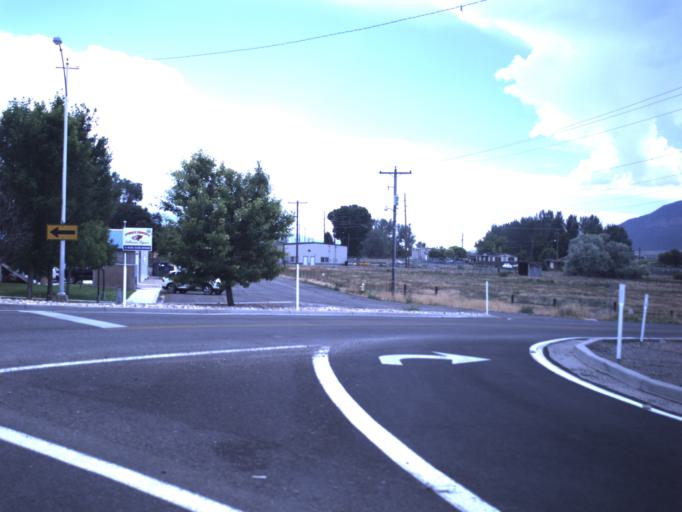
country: US
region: Utah
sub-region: Sanpete County
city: Moroni
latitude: 39.5252
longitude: -111.5904
